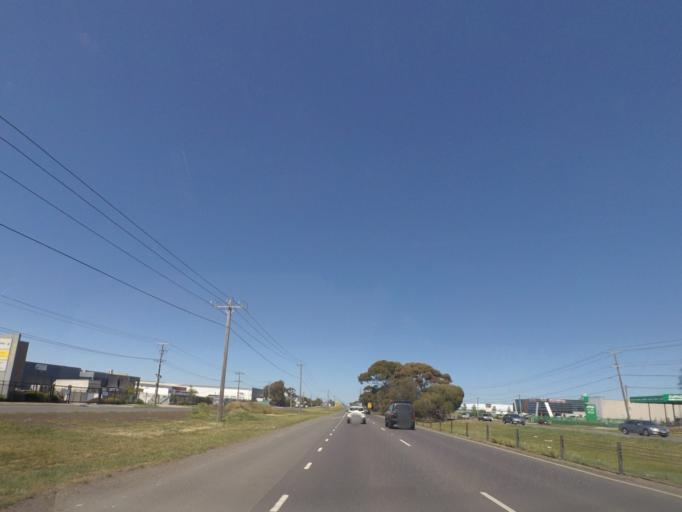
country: AU
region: Victoria
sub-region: Hume
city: Roxburgh Park
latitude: -37.6349
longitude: 144.9501
